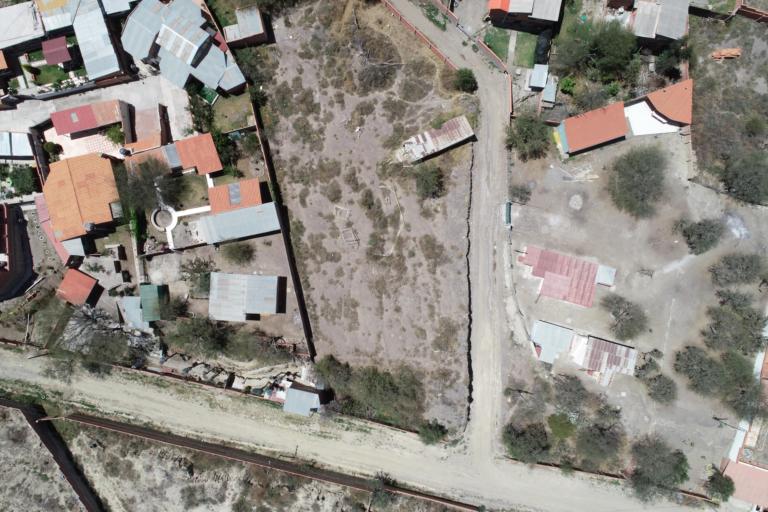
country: BO
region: La Paz
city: La Paz
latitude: -16.6439
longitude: -68.0441
